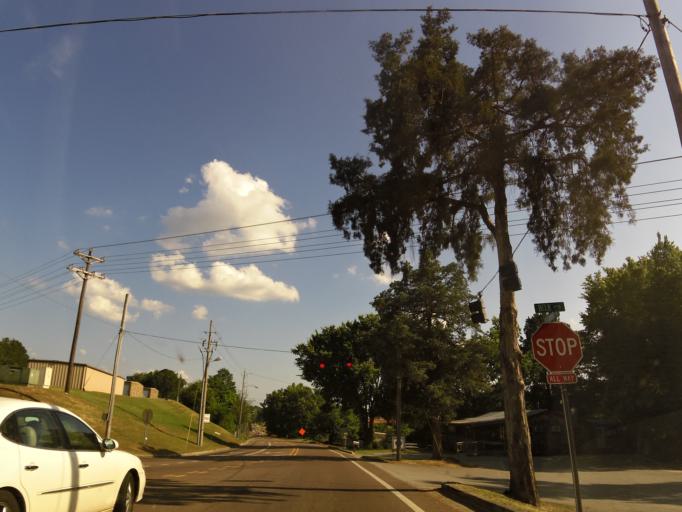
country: US
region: Mississippi
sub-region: Lafayette County
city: University
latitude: 34.3469
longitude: -89.5213
